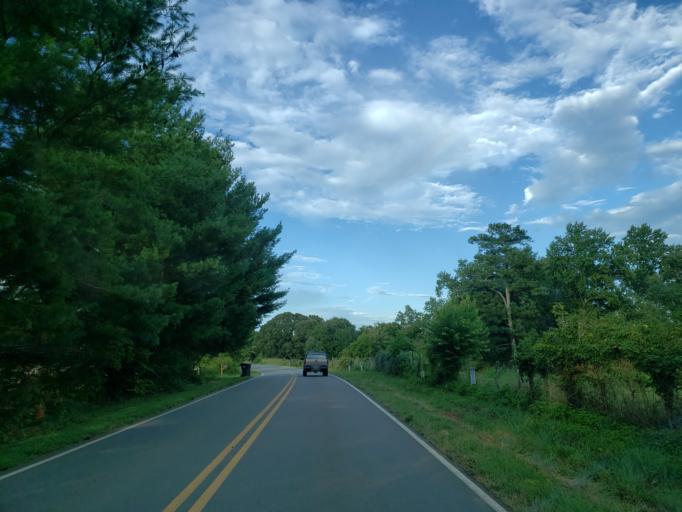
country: US
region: Georgia
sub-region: Cherokee County
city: Ball Ground
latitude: 34.3301
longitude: -84.4583
